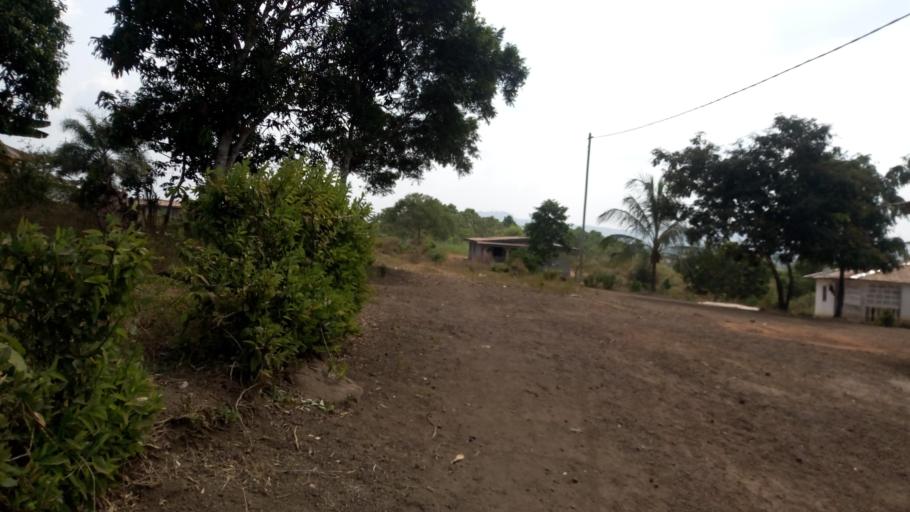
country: SL
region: Southern Province
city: Mogbwemo
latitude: 7.7810
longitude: -12.3013
